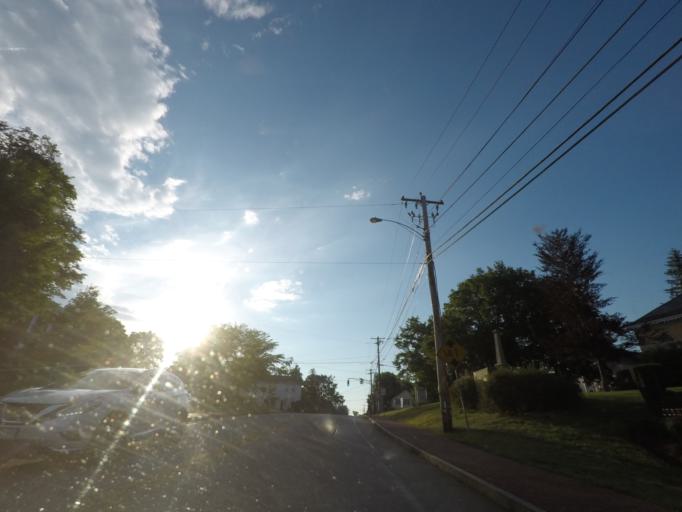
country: US
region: Massachusetts
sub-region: Worcester County
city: Sturbridge
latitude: 42.1079
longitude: -72.0802
